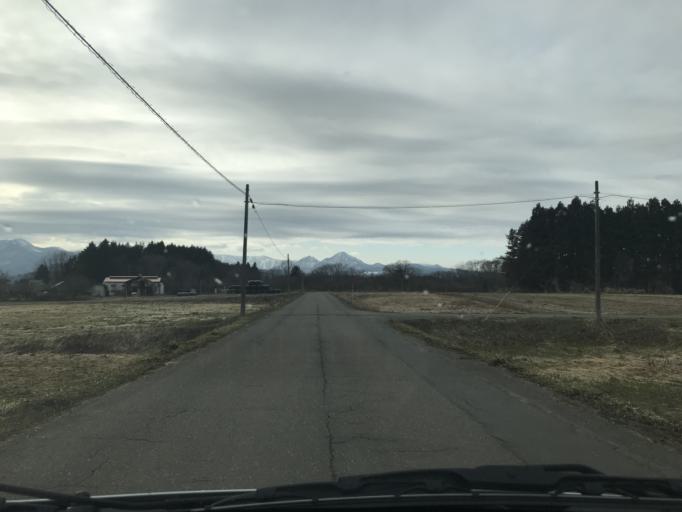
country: JP
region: Iwate
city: Kitakami
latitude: 39.2154
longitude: 141.0585
